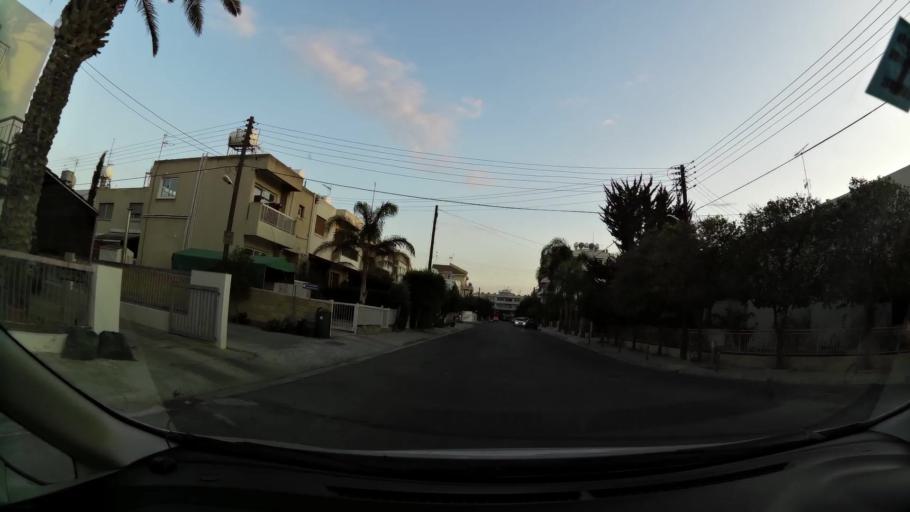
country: CY
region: Lefkosia
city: Nicosia
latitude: 35.1506
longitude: 33.3884
